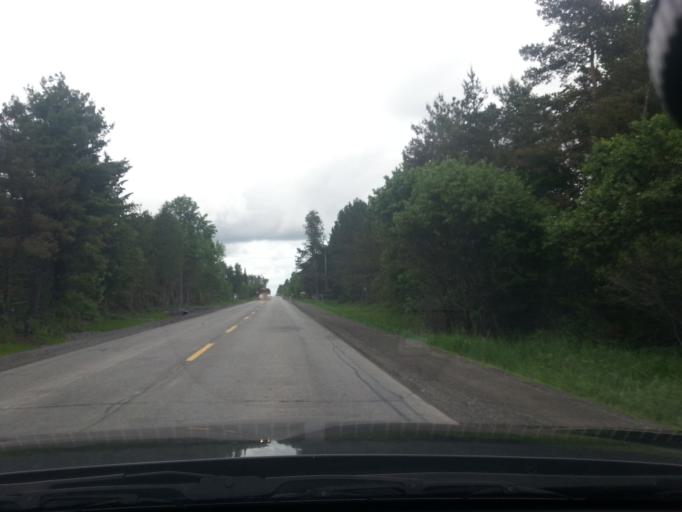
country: CA
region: Ontario
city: Bells Corners
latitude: 45.2312
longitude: -75.9126
